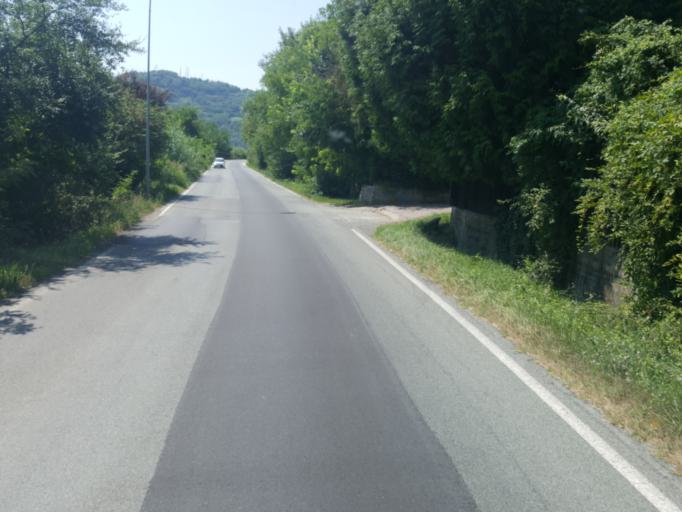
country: IT
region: Piedmont
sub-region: Provincia di Alessandria
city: Acqui Terme
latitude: 44.6784
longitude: 8.4830
